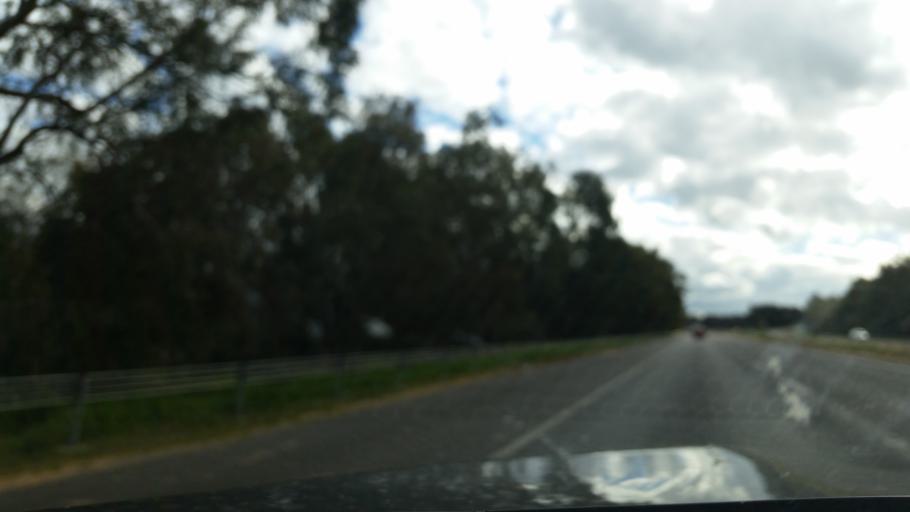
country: AU
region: Victoria
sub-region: Wodonga
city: Wodonga
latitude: -36.1091
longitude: 146.8776
